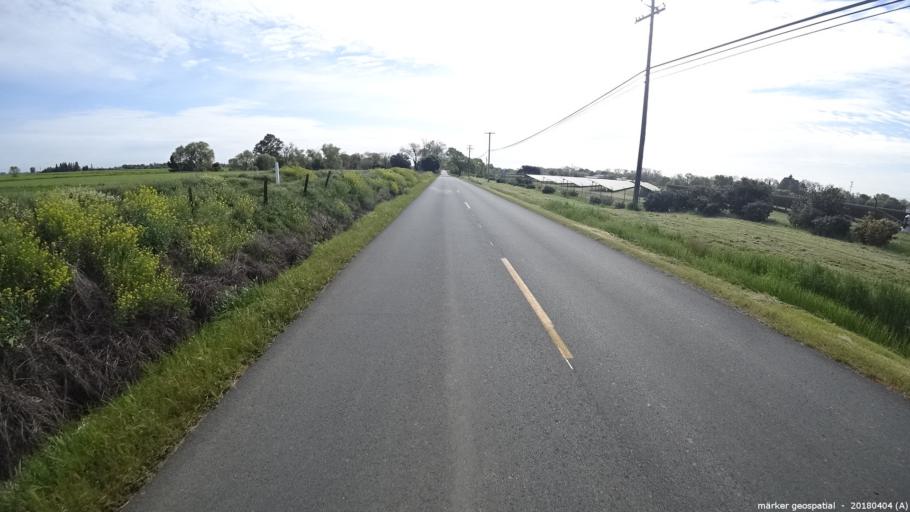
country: US
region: California
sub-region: Sacramento County
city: Galt
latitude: 38.2550
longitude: -121.2803
